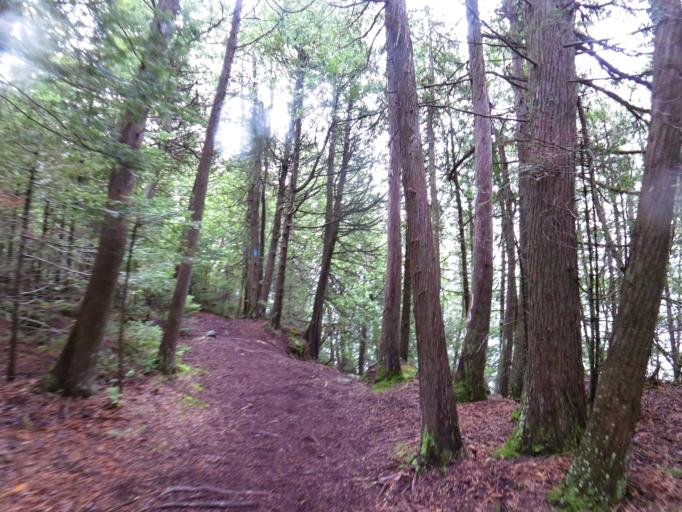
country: CA
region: Ontario
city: Tobermory
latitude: 45.2588
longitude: -81.6463
